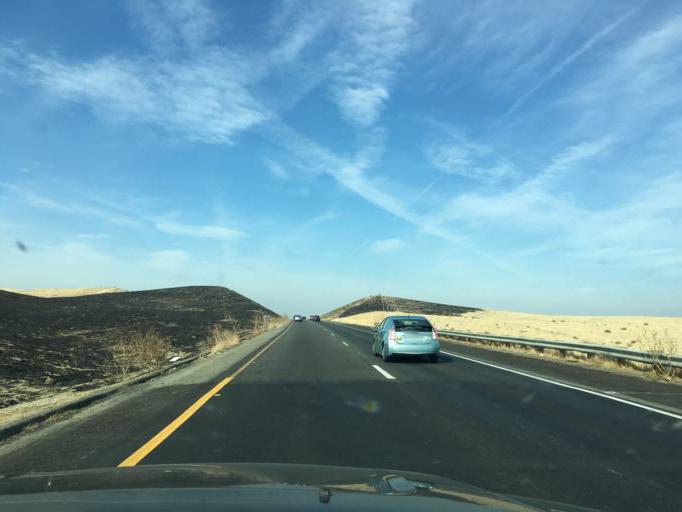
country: US
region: California
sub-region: Fresno County
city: Coalinga
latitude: 36.3186
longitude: -120.2887
